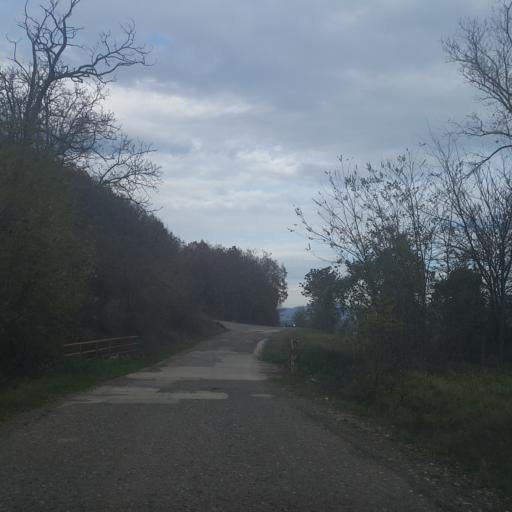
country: RS
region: Central Serbia
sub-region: Zajecarski Okrug
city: Knjazevac
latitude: 43.6080
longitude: 22.2585
